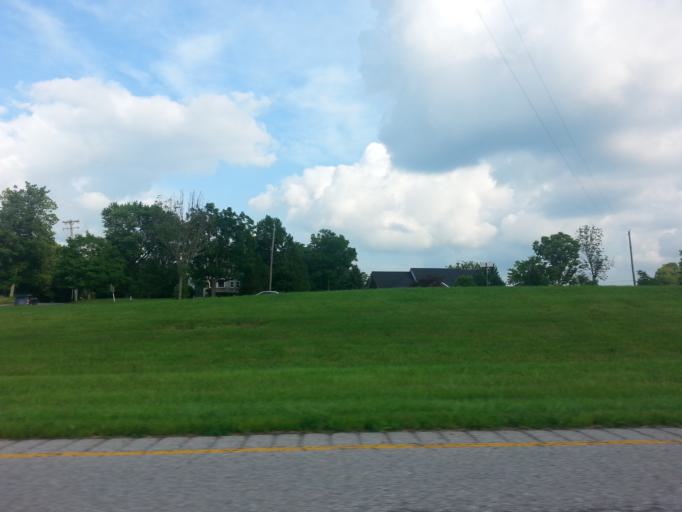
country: US
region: Kentucky
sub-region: Bourbon County
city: Paris
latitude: 38.1441
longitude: -84.3533
